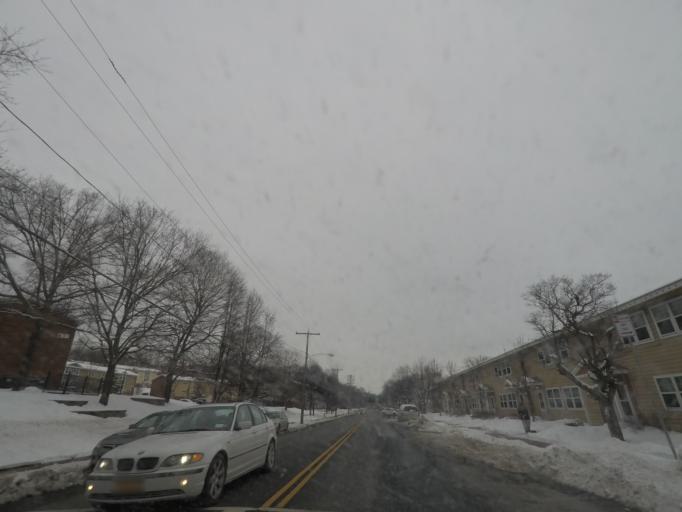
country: US
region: New York
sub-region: Albany County
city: Albany
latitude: 42.6302
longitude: -73.7658
